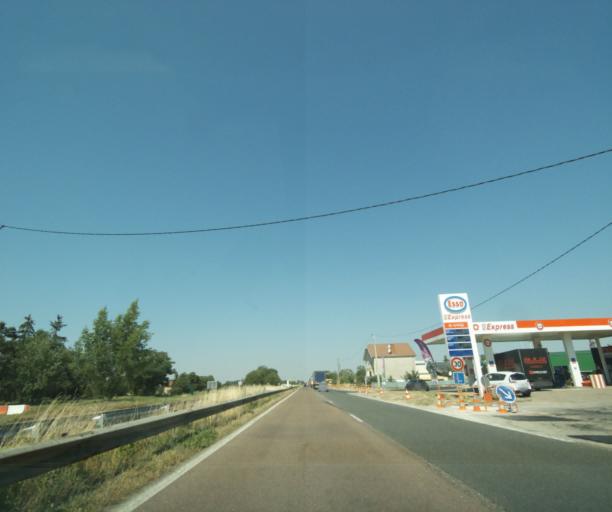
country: FR
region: Champagne-Ardenne
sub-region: Departement de la Haute-Marne
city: Villiers-en-Lieu
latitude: 48.6414
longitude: 4.9078
